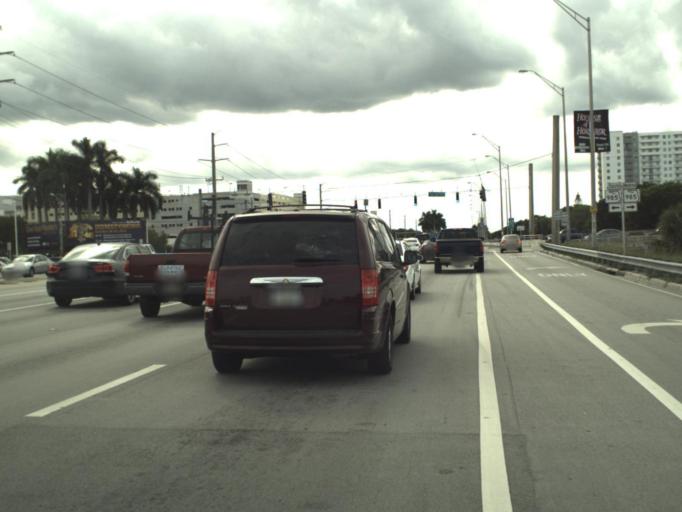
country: US
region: Florida
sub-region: Miami-Dade County
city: Sweetwater
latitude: 25.7615
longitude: -80.3674
